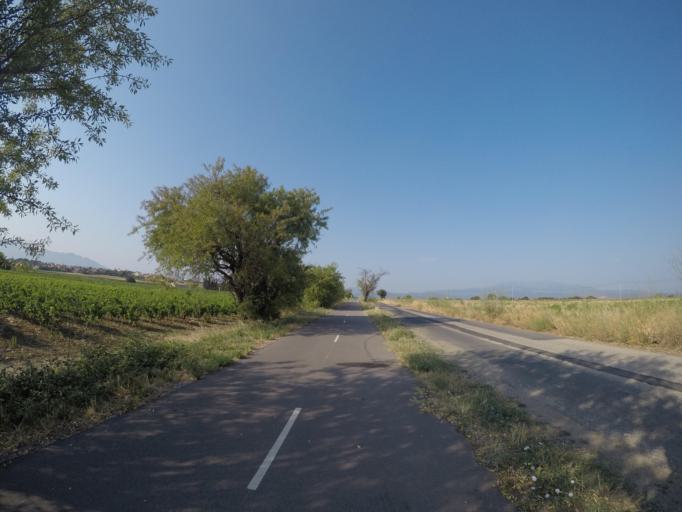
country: FR
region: Languedoc-Roussillon
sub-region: Departement des Pyrenees-Orientales
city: Ponteilla
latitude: 42.6361
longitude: 2.8094
